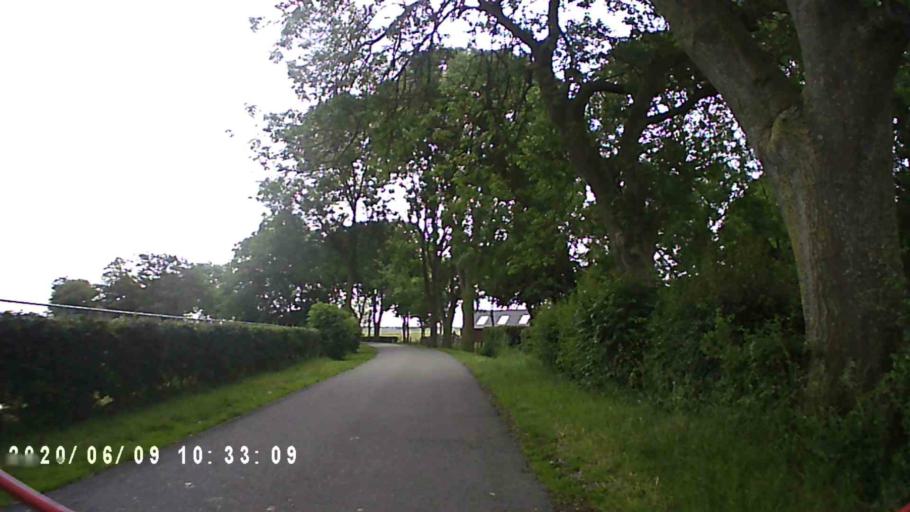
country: NL
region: Groningen
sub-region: Gemeente Zuidhorn
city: Aduard
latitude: 53.2675
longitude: 6.5119
